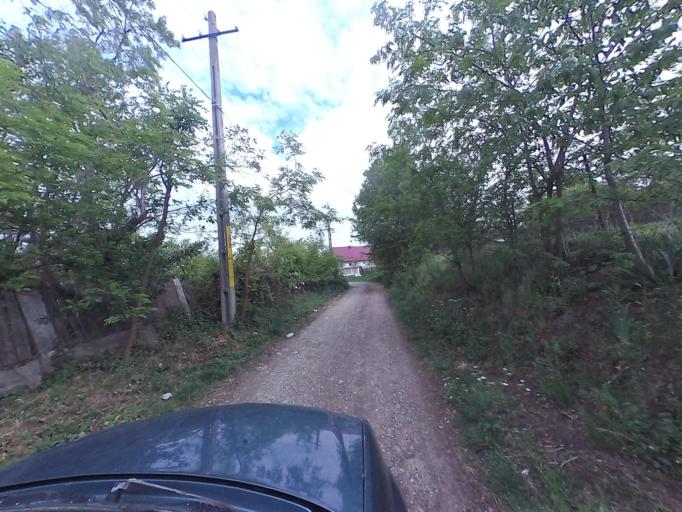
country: RO
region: Neamt
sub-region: Comuna Dulcesti
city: Dulcesti
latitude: 46.9566
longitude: 26.7912
